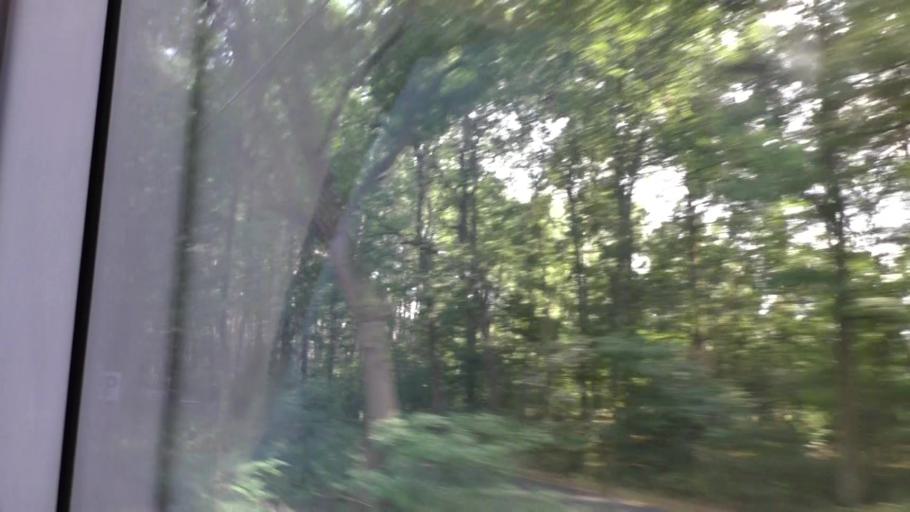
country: DE
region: Brandenburg
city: Bestensee
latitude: 52.2984
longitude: 13.7402
